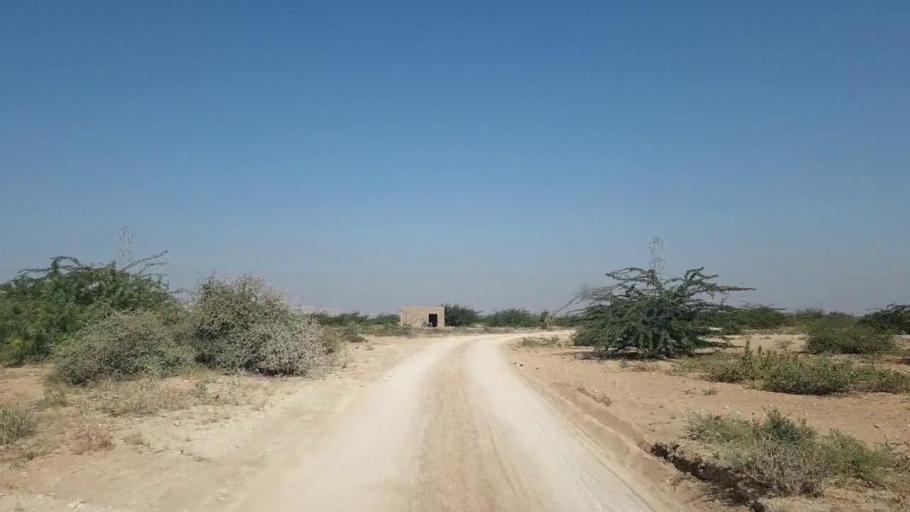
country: PK
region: Sindh
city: Gharo
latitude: 25.1929
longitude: 67.7411
